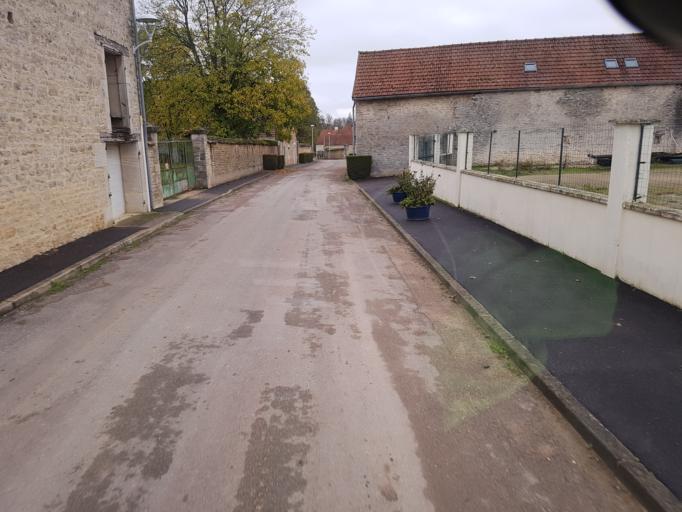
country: FR
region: Bourgogne
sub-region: Departement de la Cote-d'Or
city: Is-sur-Tille
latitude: 47.5339
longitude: 4.9824
